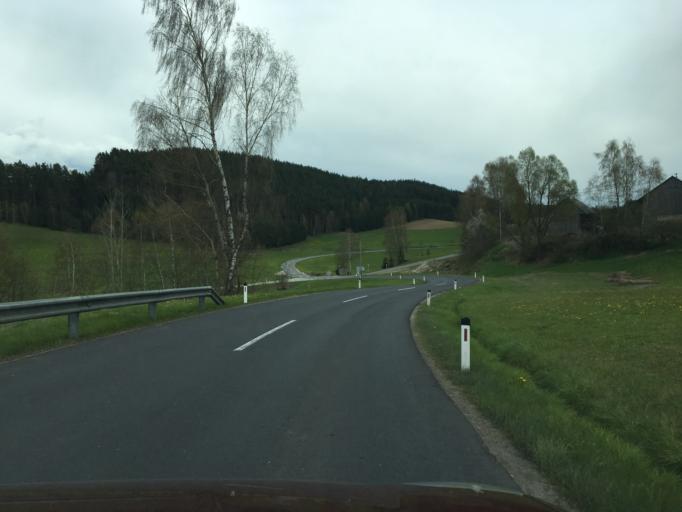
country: AT
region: Upper Austria
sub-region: Politischer Bezirk Urfahr-Umgebung
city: Reichenthal
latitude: 48.5450
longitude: 14.3939
